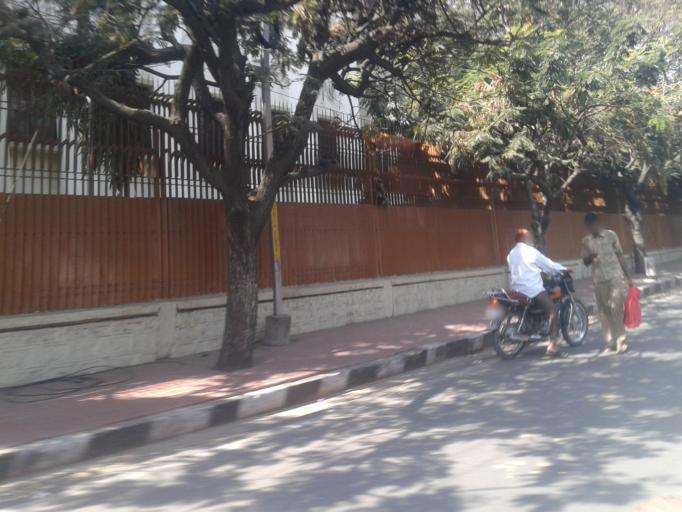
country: IN
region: Telangana
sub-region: Hyderabad
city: Hyderabad
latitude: 17.4054
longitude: 78.4673
